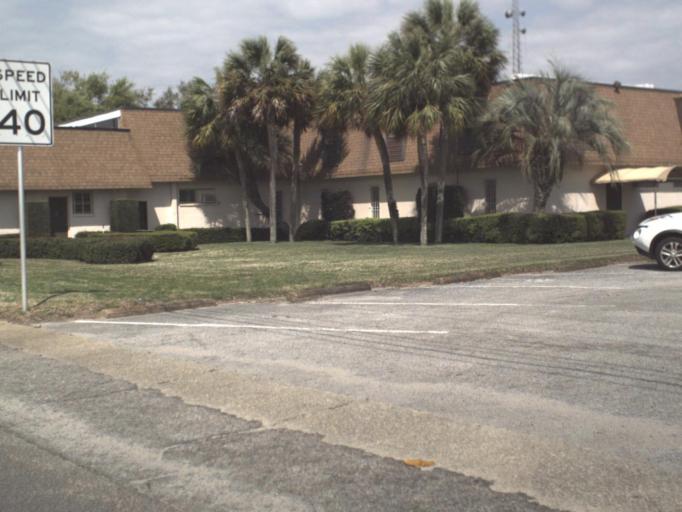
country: US
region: Florida
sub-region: Escambia County
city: Warrington
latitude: 30.3886
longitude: -87.2740
